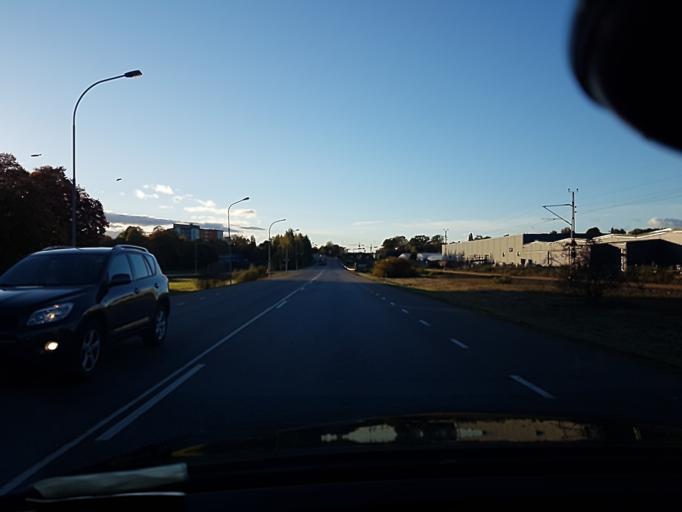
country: SE
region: Kronoberg
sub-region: Vaxjo Kommun
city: Vaexjoe
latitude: 56.8702
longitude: 14.8266
